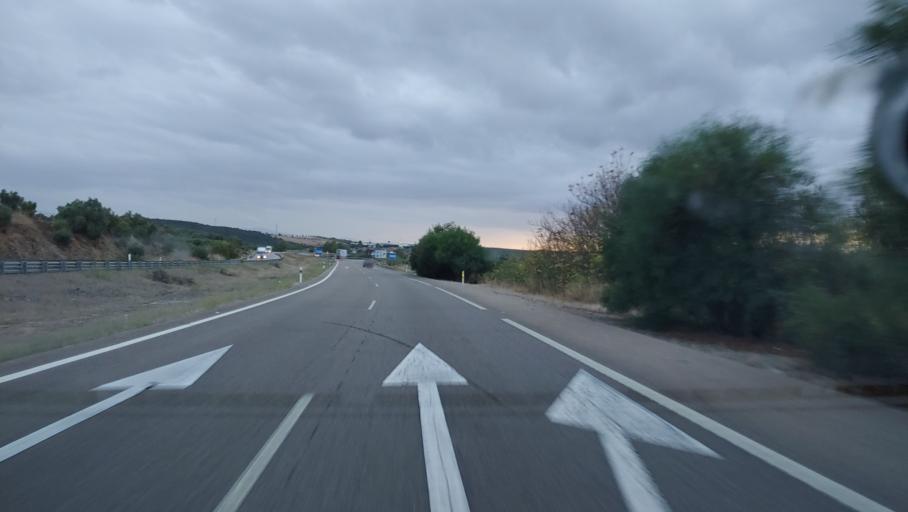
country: ES
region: Andalusia
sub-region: Provincia de Jaen
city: Guarroman
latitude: 38.1724
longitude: -3.7063
